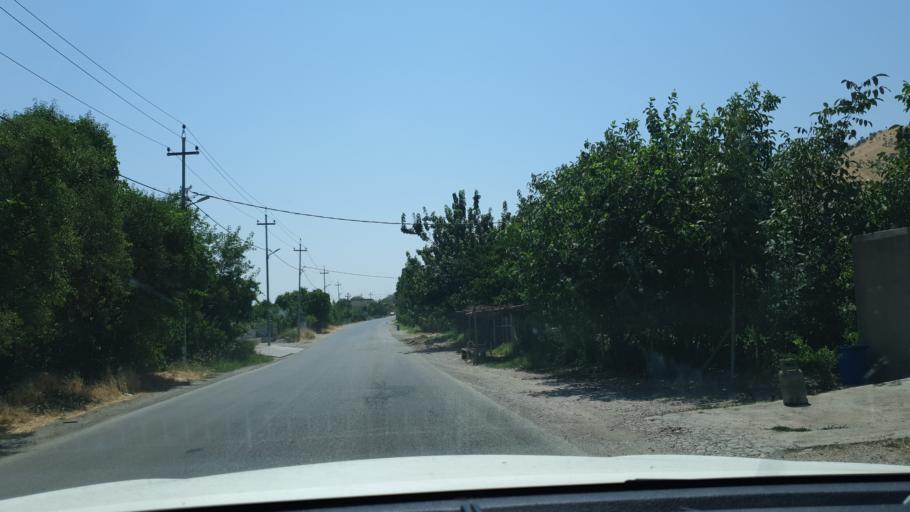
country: IQ
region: Arbil
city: Nahiyat Hiran
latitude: 36.2974
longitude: 44.4726
